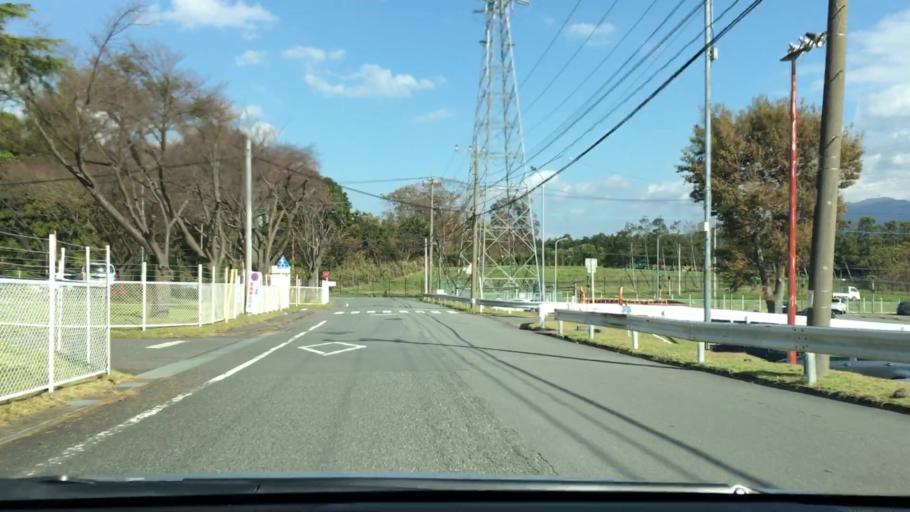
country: JP
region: Shizuoka
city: Gotemba
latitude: 35.2289
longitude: 138.8892
